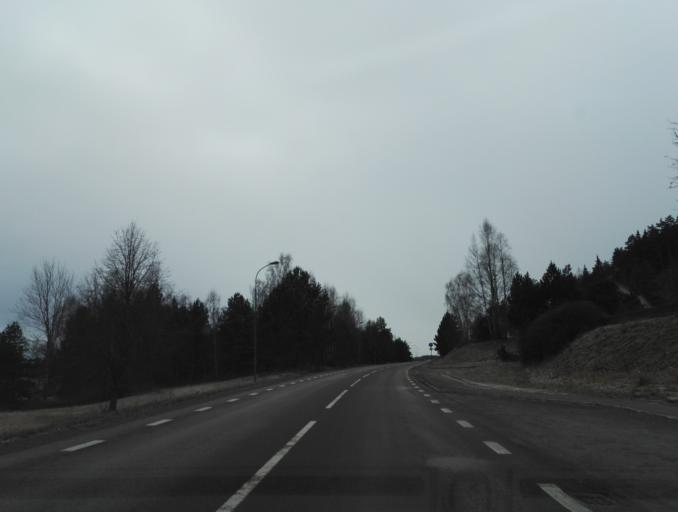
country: SE
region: Kalmar
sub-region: Hultsfreds Kommun
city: Virserum
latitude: 57.3258
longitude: 15.5846
